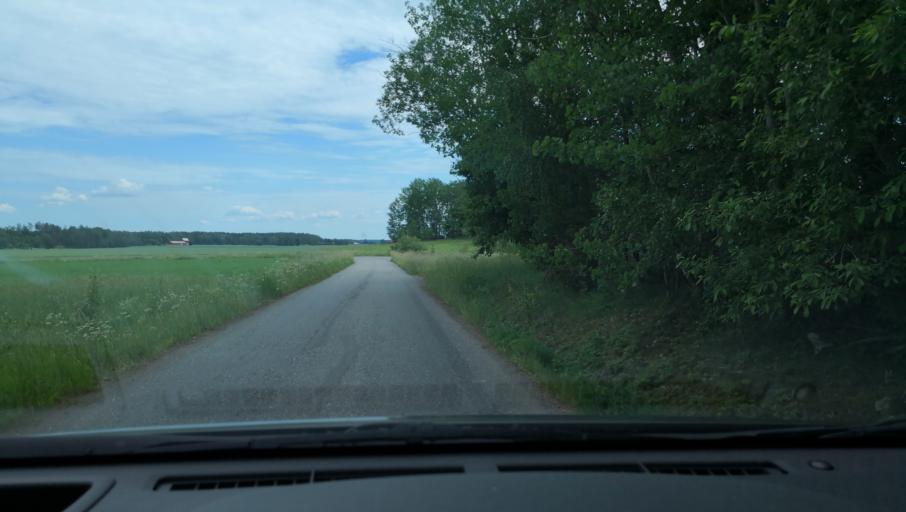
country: SE
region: Uppsala
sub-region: Enkopings Kommun
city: Orsundsbro
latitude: 59.6968
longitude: 17.4057
